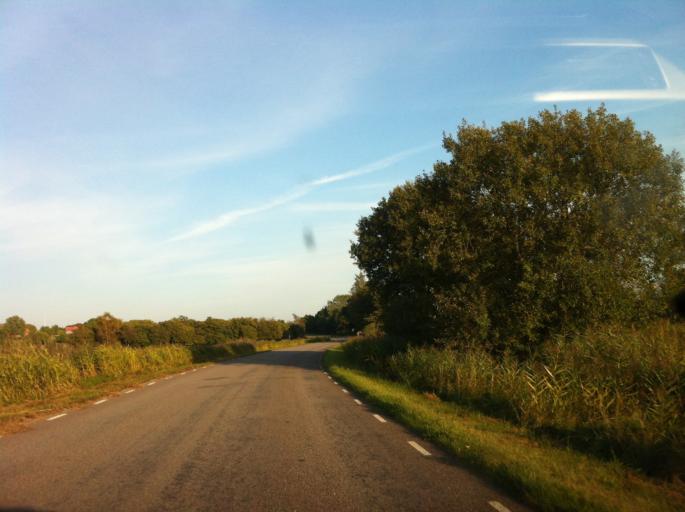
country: SE
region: Gotland
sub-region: Gotland
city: Slite
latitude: 57.4191
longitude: 18.8736
